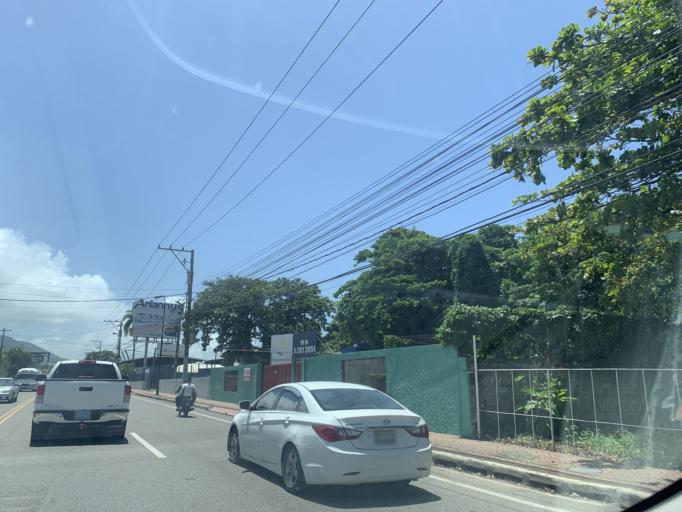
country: DO
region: Puerto Plata
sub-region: Puerto Plata
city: Puerto Plata
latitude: 19.7771
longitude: -70.6625
